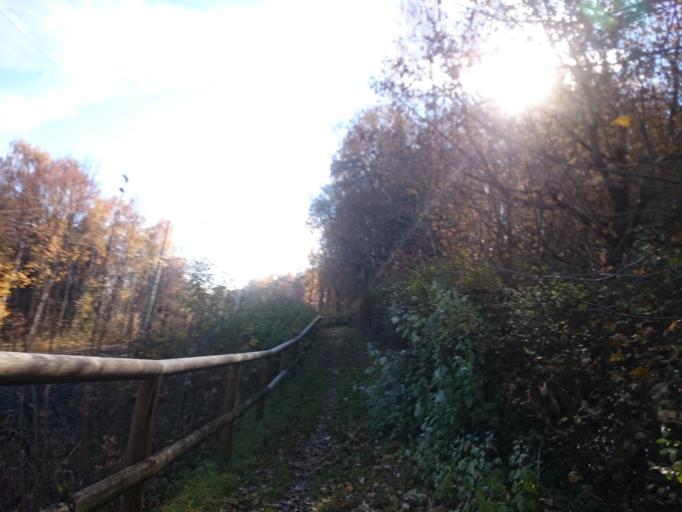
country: DE
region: Bavaria
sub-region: Upper Franconia
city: Hof
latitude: 50.3240
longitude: 11.9038
